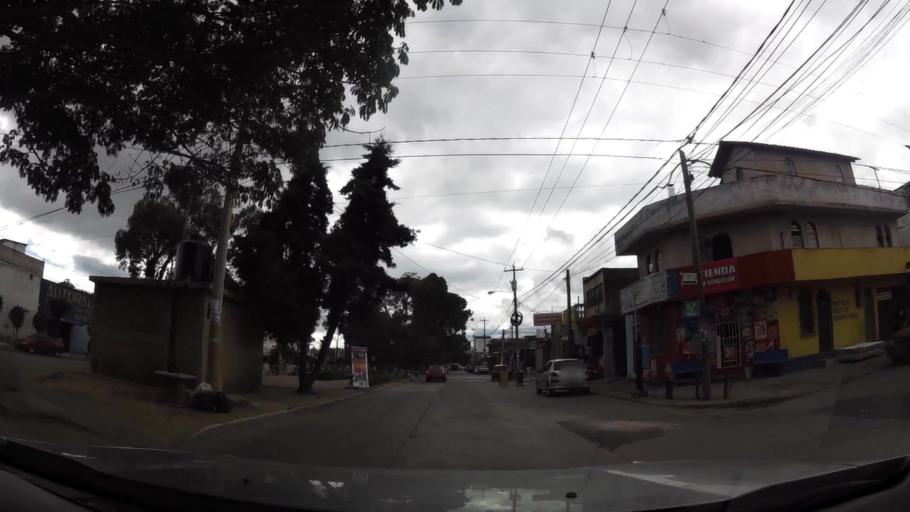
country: GT
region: Guatemala
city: Mixco
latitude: 14.6530
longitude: -90.5747
